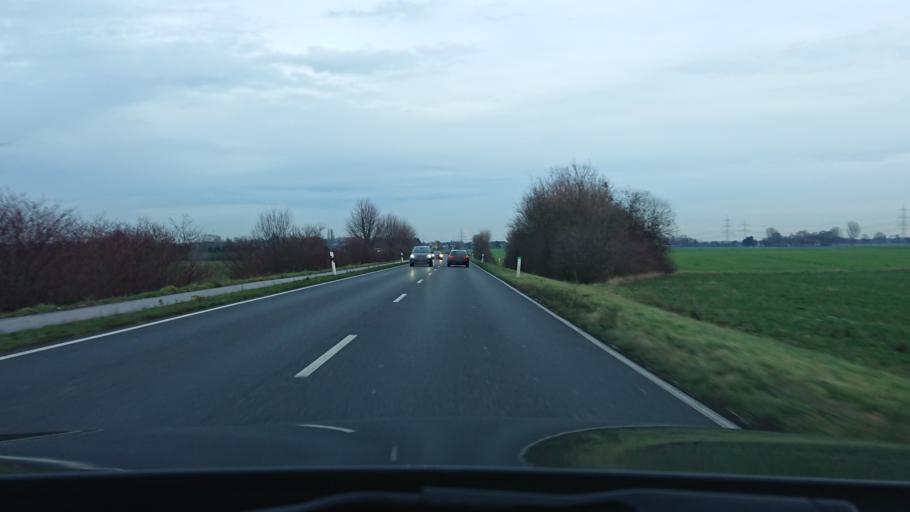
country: DE
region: North Rhine-Westphalia
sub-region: Regierungsbezirk Koln
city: Sinnersdorf
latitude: 51.0230
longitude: 6.7967
